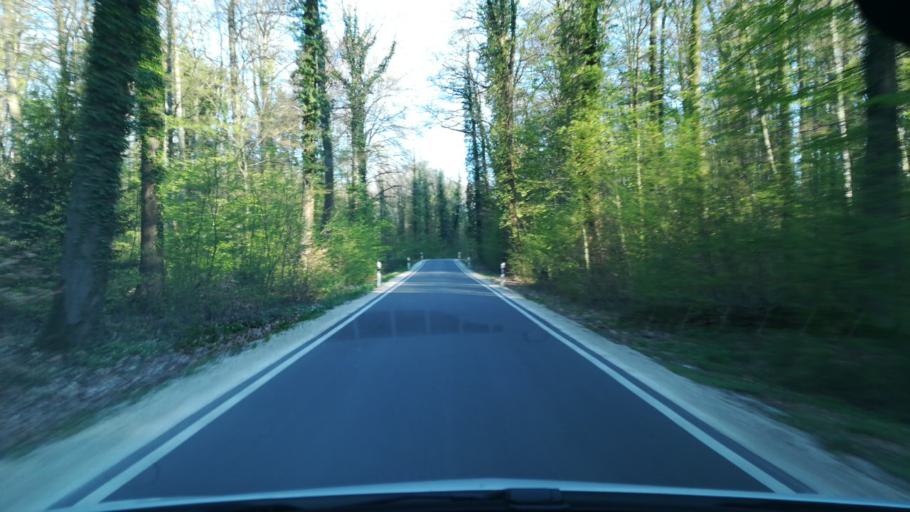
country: DE
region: Baden-Wuerttemberg
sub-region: Freiburg Region
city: Singen
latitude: 47.7720
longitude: 8.8556
